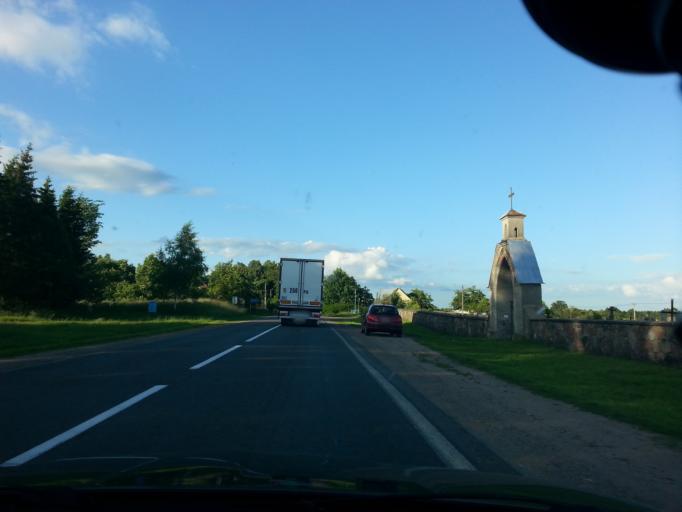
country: BY
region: Minsk
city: Svir
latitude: 54.9131
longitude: 26.4436
